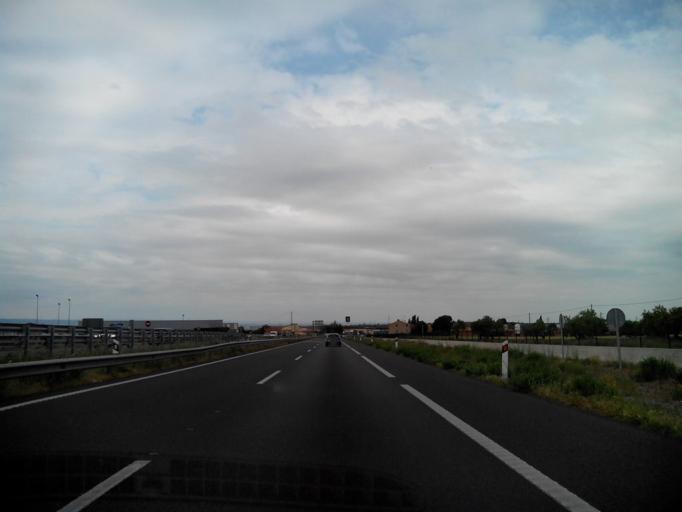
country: ES
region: Catalonia
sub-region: Provincia de Lleida
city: Cervera
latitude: 41.6646
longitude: 1.2073
